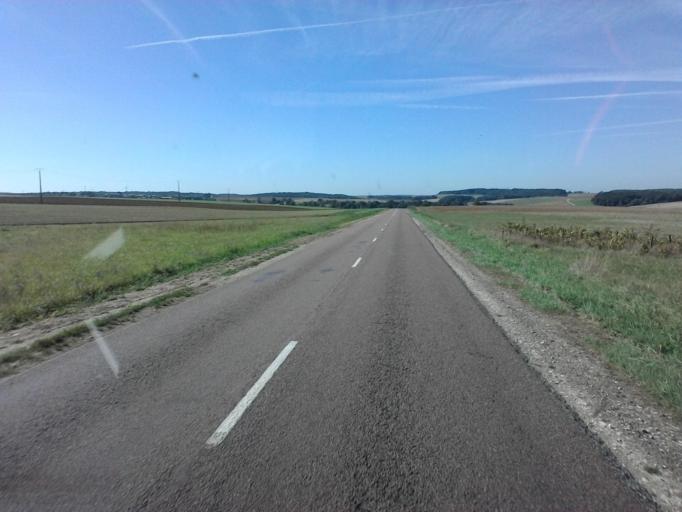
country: FR
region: Bourgogne
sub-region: Departement de l'Yonne
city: Tonnerre
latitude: 47.9633
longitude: 4.0290
